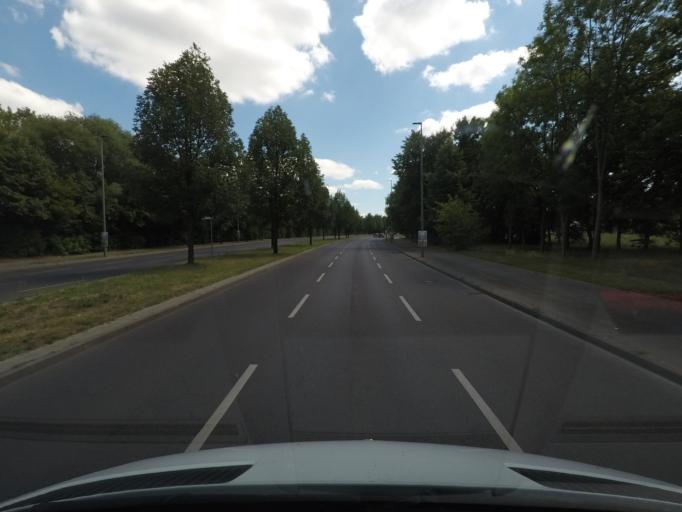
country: DE
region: Berlin
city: Biesdorf
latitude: 52.5203
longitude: 13.5428
